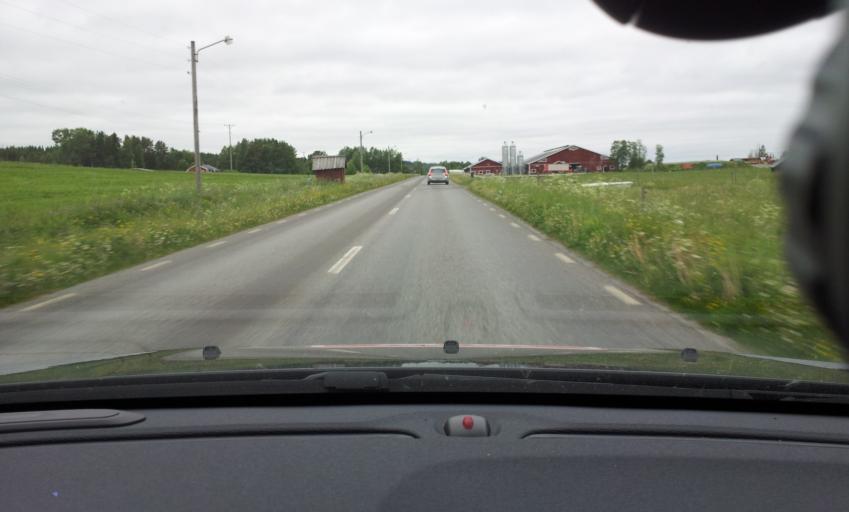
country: SE
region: Jaemtland
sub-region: Krokoms Kommun
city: Krokom
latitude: 63.1636
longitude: 14.1230
